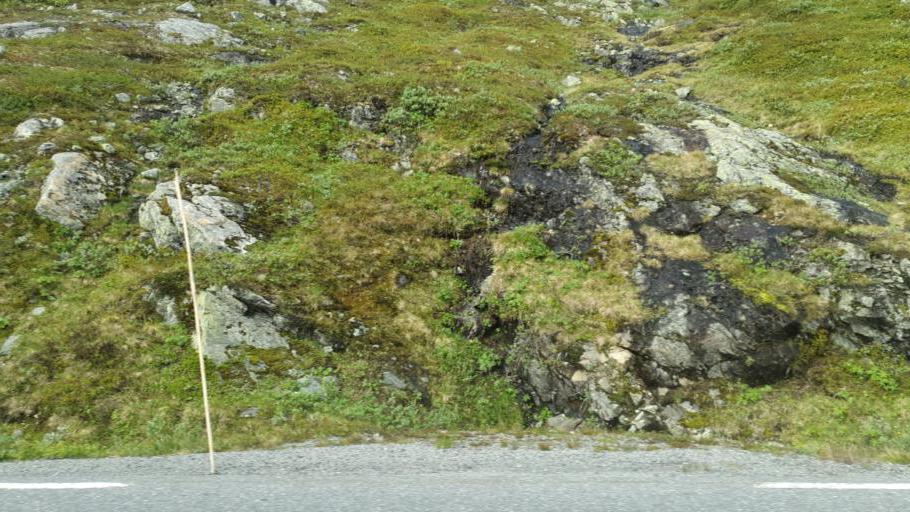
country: NO
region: Oppland
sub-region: Vestre Slidre
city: Slidre
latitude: 61.3391
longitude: 8.8151
